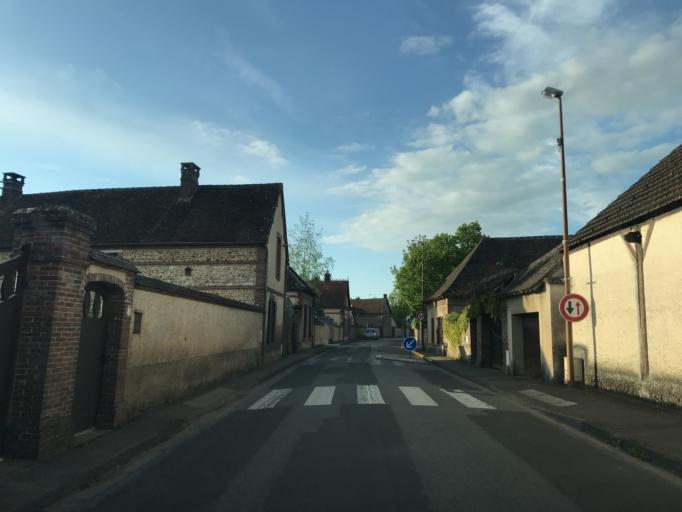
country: FR
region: Haute-Normandie
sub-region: Departement de l'Eure
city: Marcilly-sur-Eure
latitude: 48.8215
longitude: 1.3432
